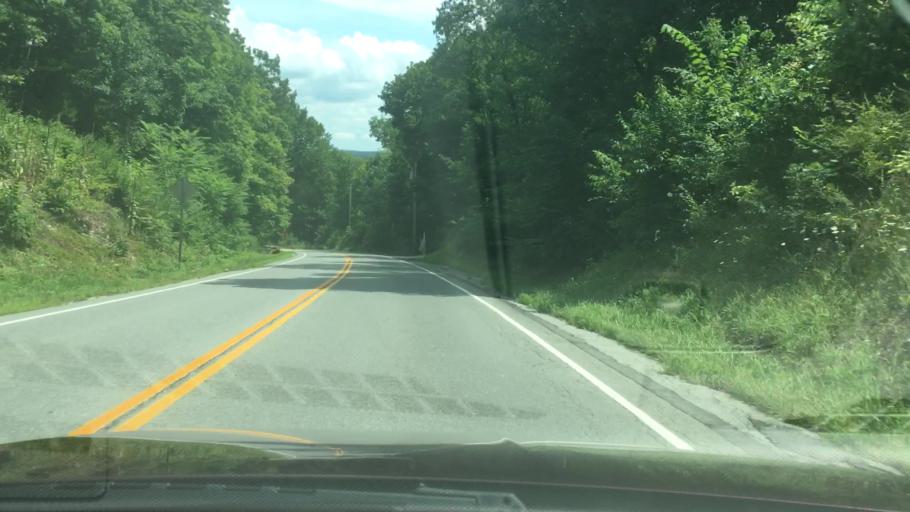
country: US
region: New York
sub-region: Dutchess County
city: Hillside Lake
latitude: 41.6453
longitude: -73.8186
